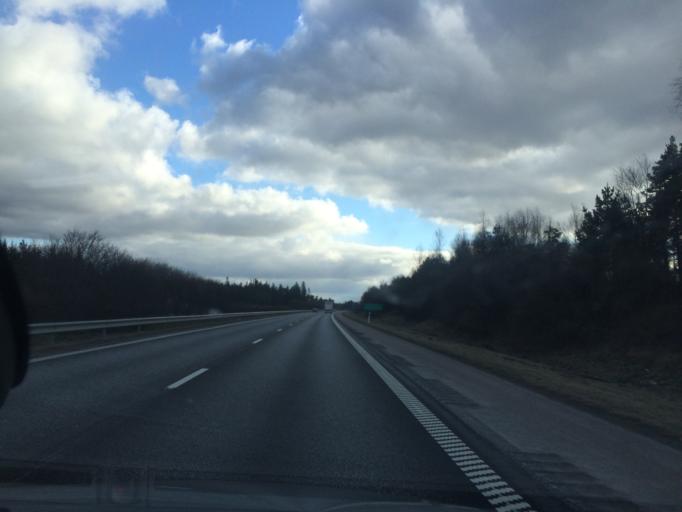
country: SE
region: Joenkoeping
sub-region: Vaggeryds Kommun
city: Skillingaryd
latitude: 57.3573
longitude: 14.1053
